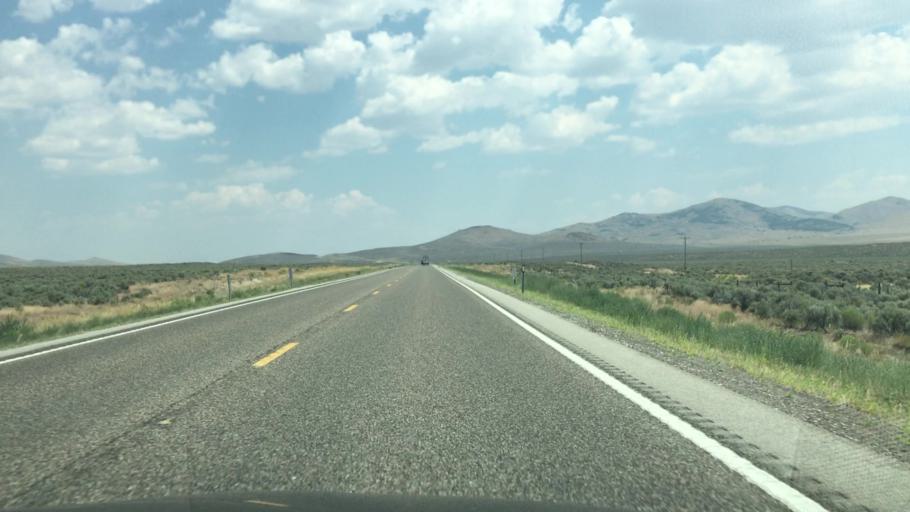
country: US
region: Nevada
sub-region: Elko County
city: Wells
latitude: 41.1559
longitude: -114.8978
